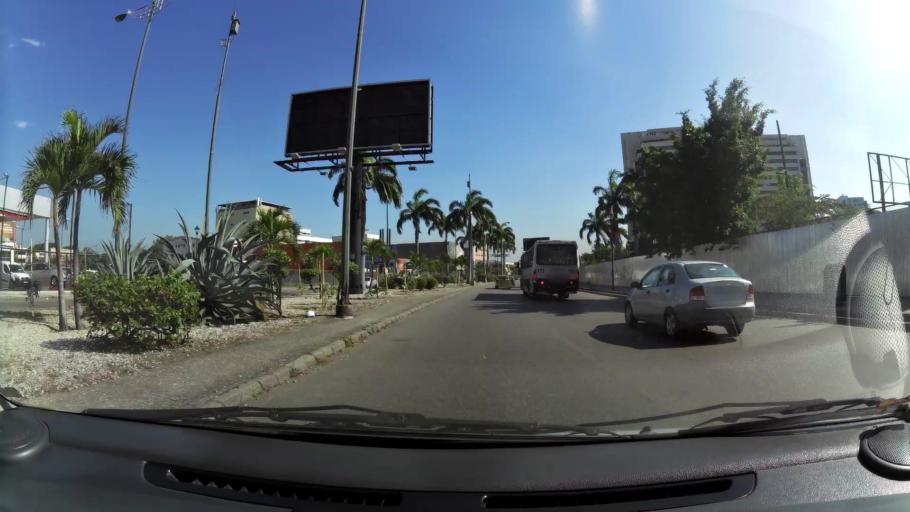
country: EC
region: Guayas
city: Guayaquil
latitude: -2.1617
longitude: -79.8984
